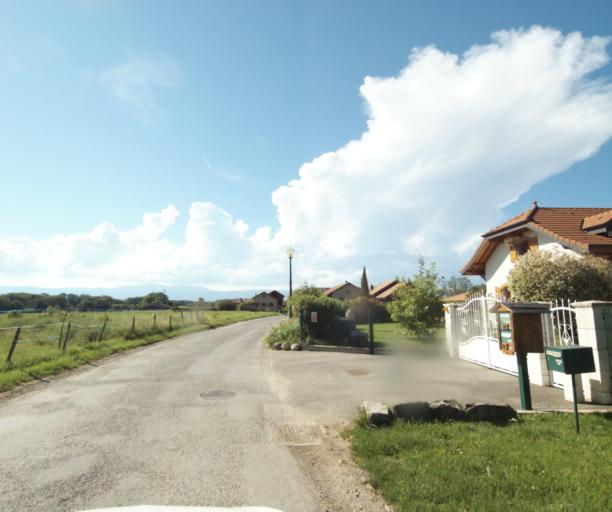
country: FR
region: Rhone-Alpes
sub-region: Departement de la Haute-Savoie
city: Massongy
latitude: 46.3231
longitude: 6.3205
